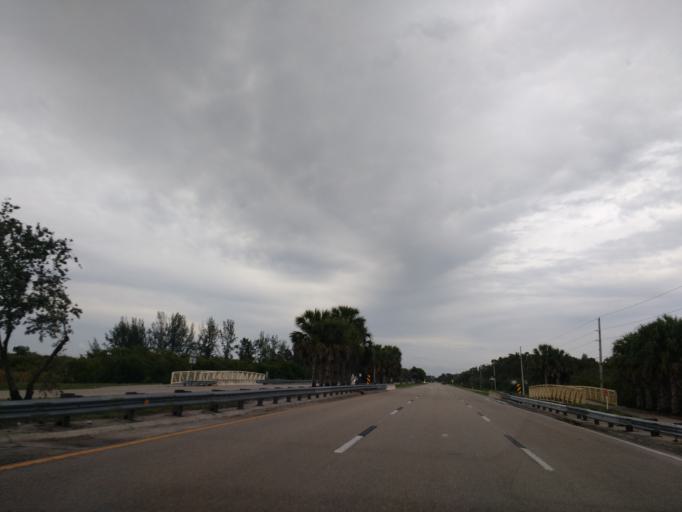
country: US
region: Florida
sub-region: Lee County
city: Harlem Heights
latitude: 26.4978
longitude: -81.9208
